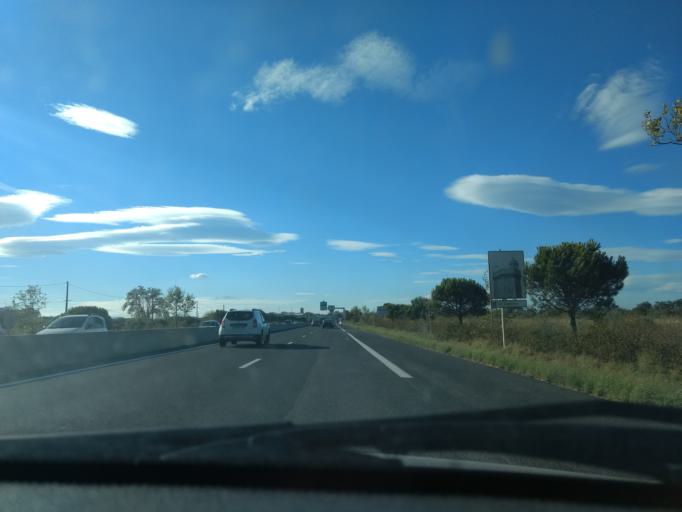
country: FR
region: Languedoc-Roussillon
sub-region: Departement des Pyrenees-Orientales
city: Villeneuve-de-la-Raho
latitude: 42.6598
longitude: 2.9234
